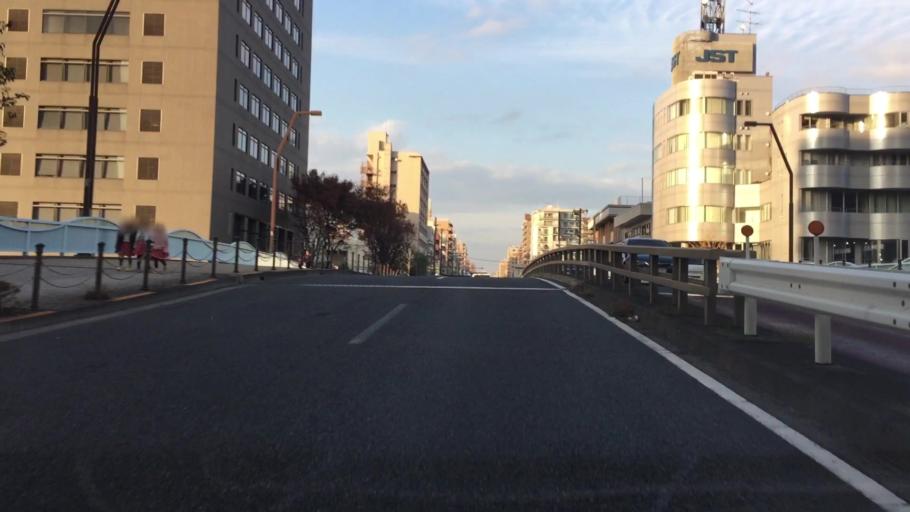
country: JP
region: Tokyo
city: Urayasu
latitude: 35.6839
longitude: 139.8064
